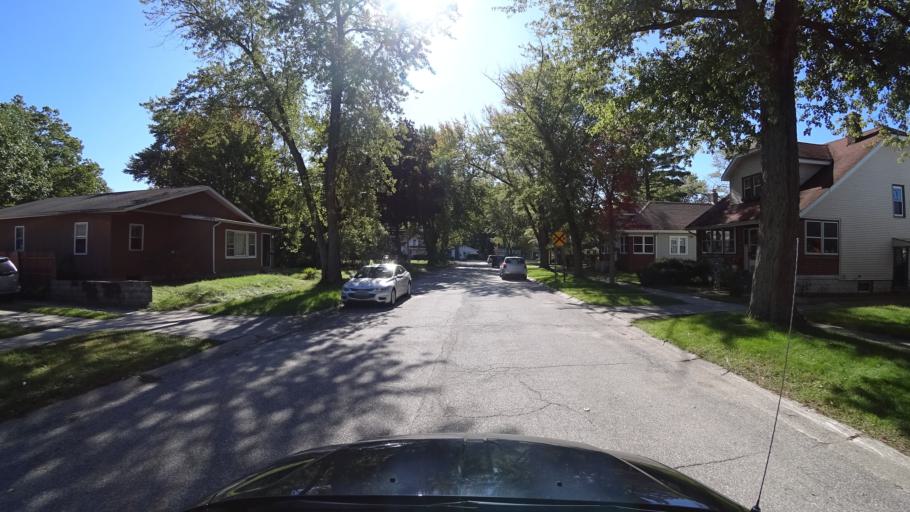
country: US
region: Indiana
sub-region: LaPorte County
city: Michigan City
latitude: 41.7081
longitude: -86.9183
